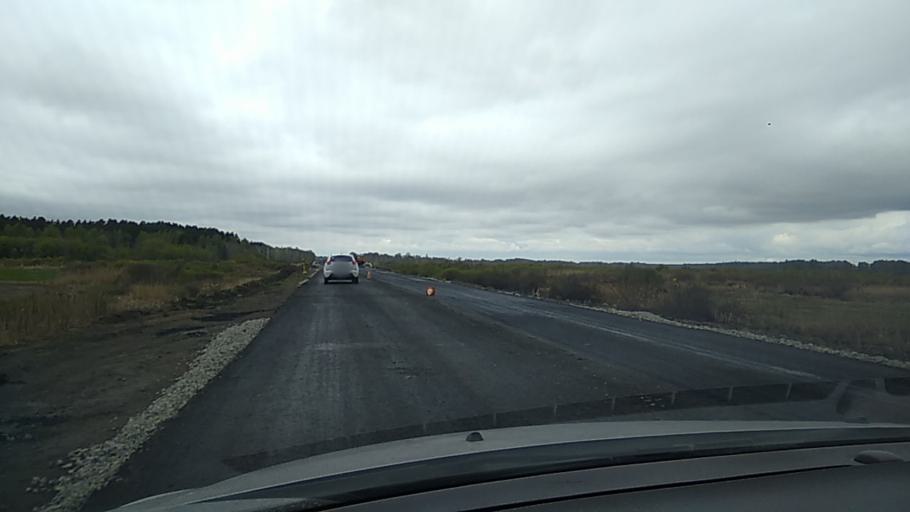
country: RU
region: Kurgan
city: Shadrinsk
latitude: 56.1530
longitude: 63.4221
